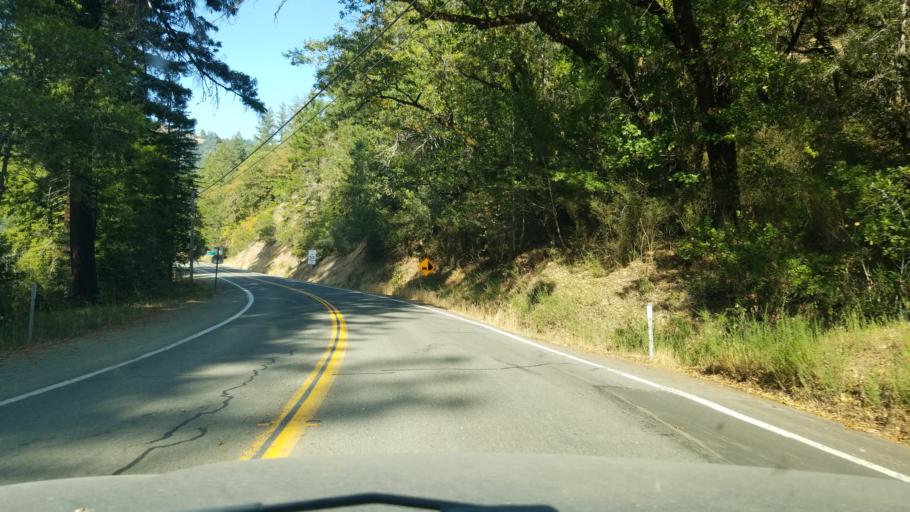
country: US
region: California
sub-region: Humboldt County
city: Redway
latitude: 40.1829
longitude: -123.7738
